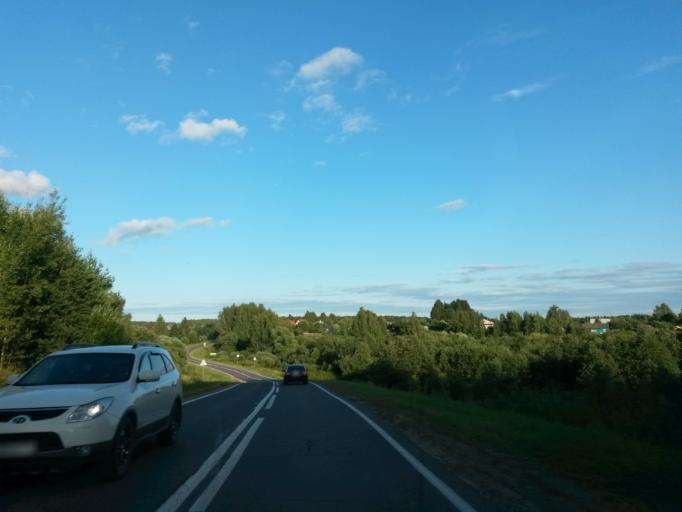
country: RU
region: Jaroslavl
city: Konstantinovskiy
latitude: 57.8065
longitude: 39.7576
